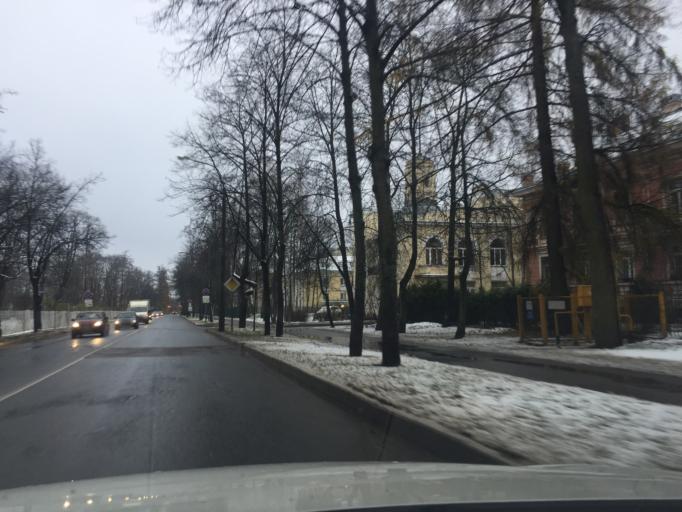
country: RU
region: St.-Petersburg
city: Pushkin
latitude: 59.7111
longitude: 30.4057
